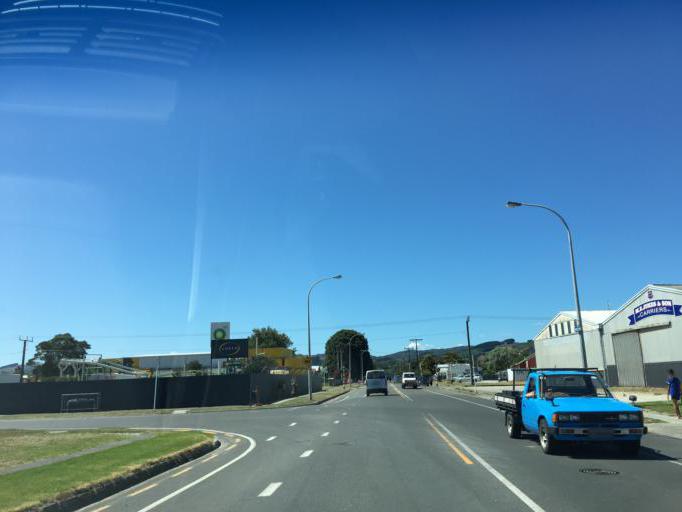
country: NZ
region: Gisborne
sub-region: Gisborne District
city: Gisborne
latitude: -38.6649
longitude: 178.0057
